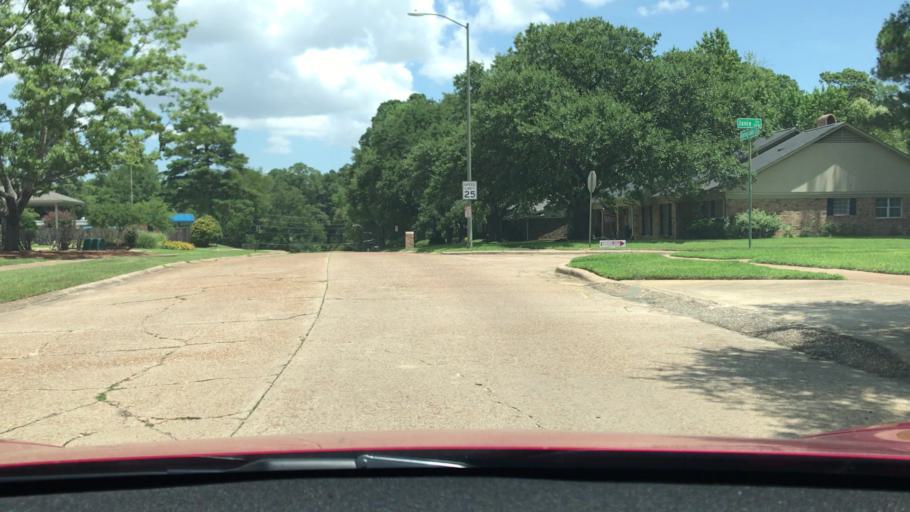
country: US
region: Louisiana
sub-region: Bossier Parish
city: Bossier City
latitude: 32.4319
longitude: -93.7365
